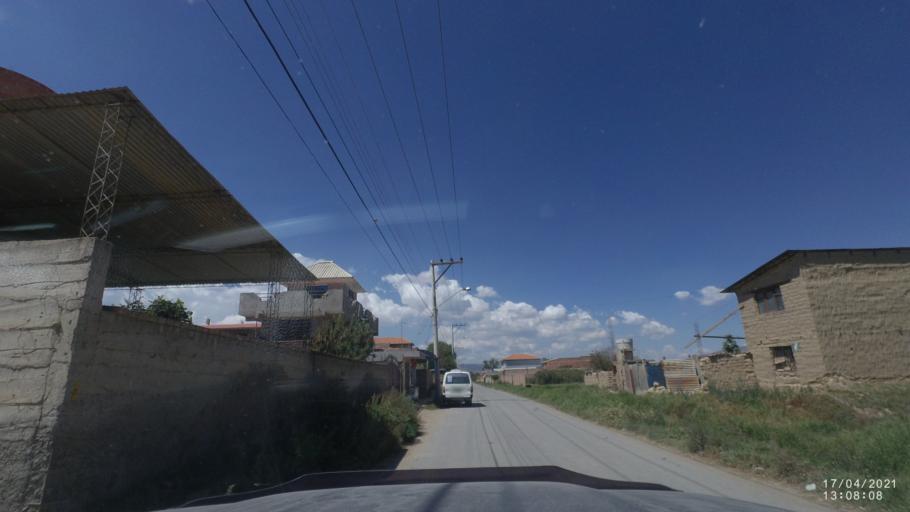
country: BO
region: Cochabamba
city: Cochabamba
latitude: -17.4142
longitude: -66.2234
